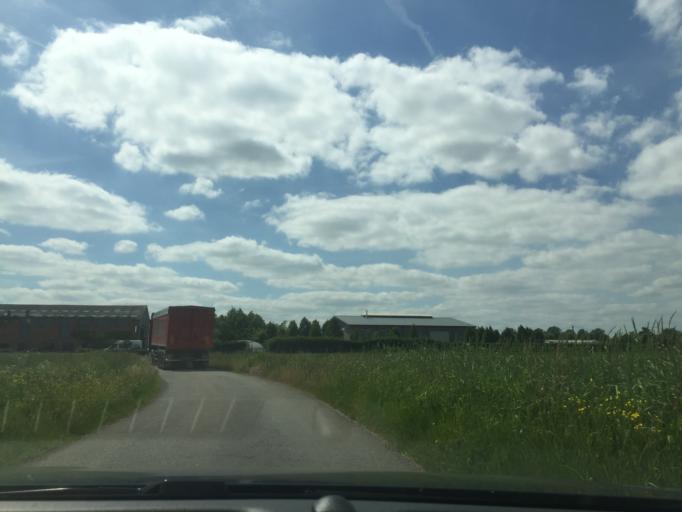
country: BE
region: Flanders
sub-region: Provincie West-Vlaanderen
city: Lendelede
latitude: 50.8720
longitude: 3.2264
